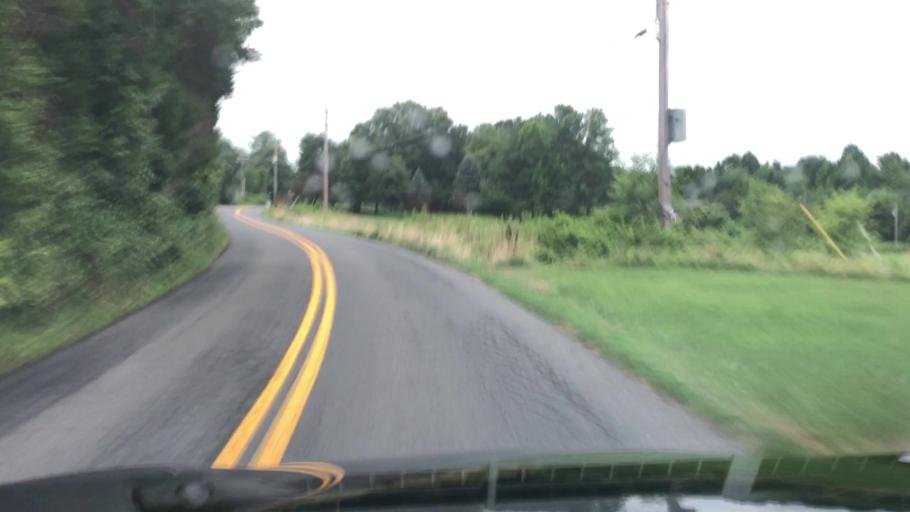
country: US
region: Virginia
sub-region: Stafford County
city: Stafford
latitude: 38.4882
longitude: -77.5823
